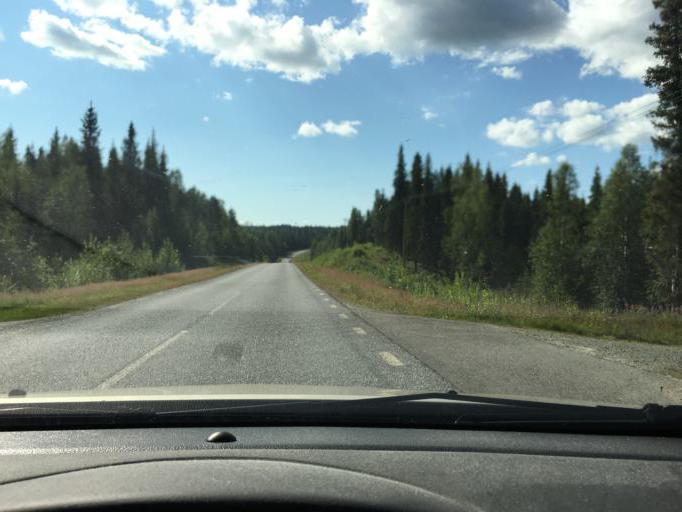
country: SE
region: Norrbotten
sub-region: Kalix Kommun
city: Toere
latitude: 66.0535
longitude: 22.5580
